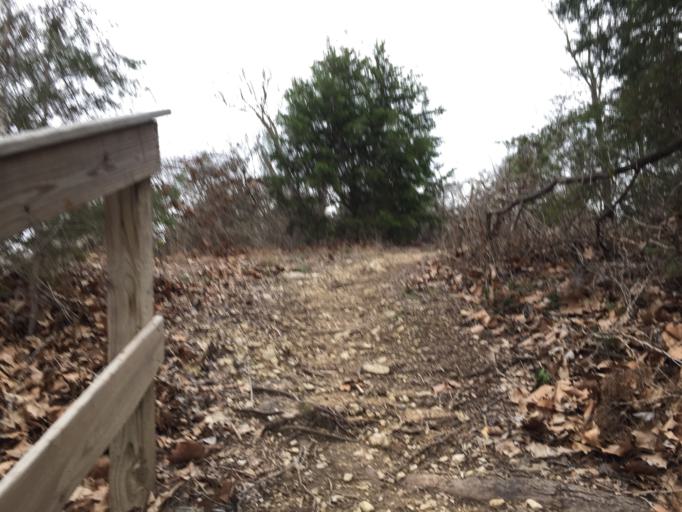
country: US
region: Texas
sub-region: Bell County
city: Fort Hood
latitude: 31.1208
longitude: -97.8171
